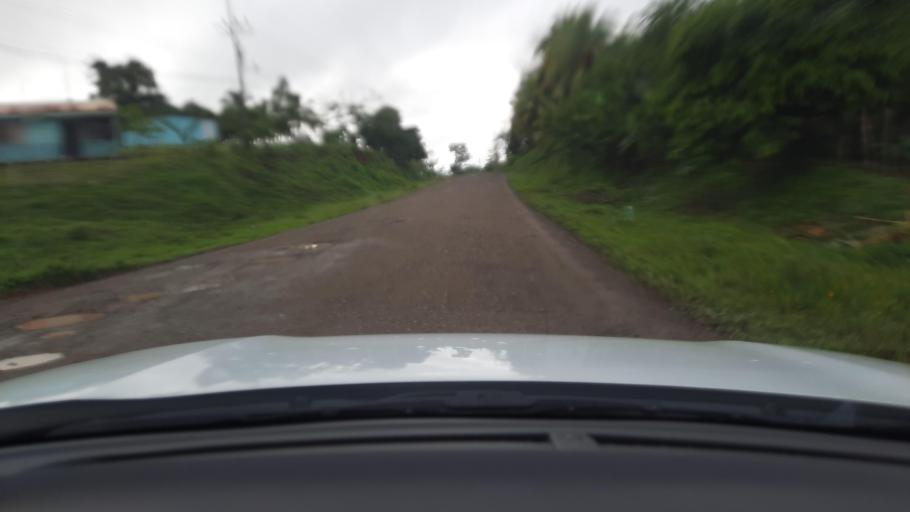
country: CR
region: Alajuela
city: San Jose
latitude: 11.0024
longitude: -85.2983
